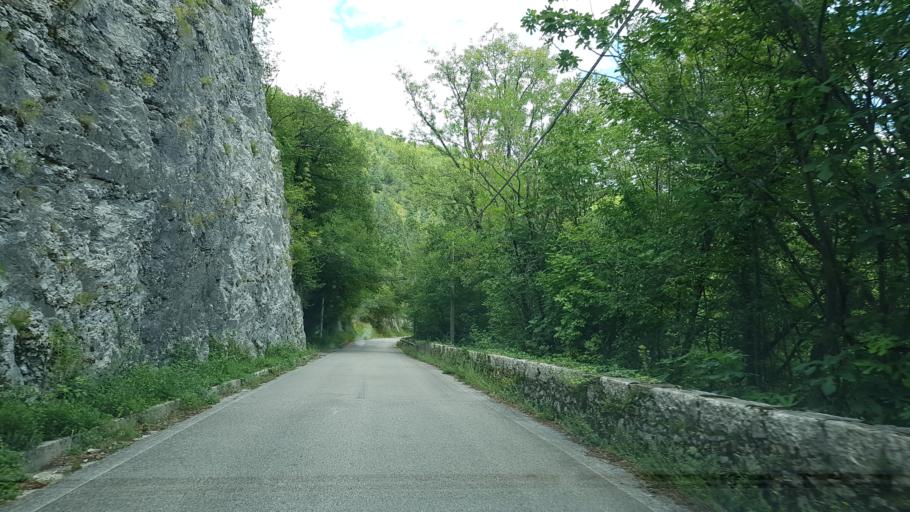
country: IT
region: Friuli Venezia Giulia
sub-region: Provincia di Udine
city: Prepotto
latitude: 46.0606
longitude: 13.5001
